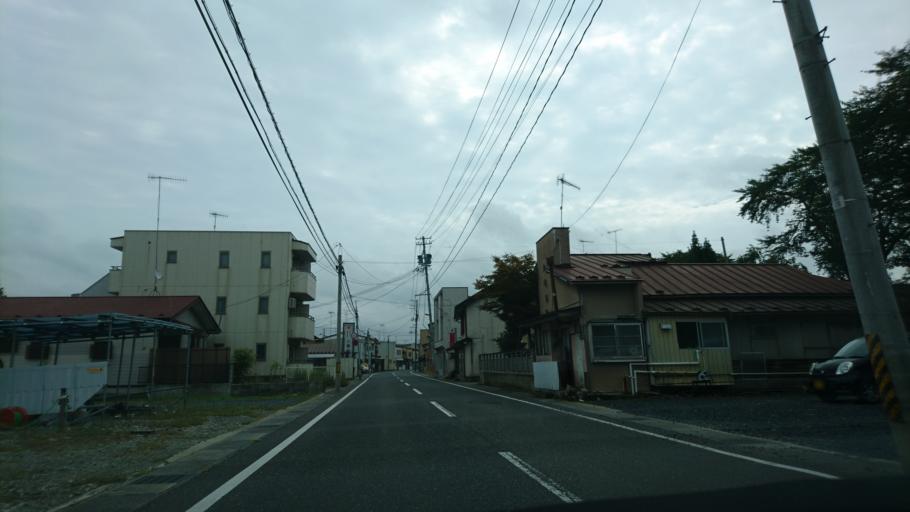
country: JP
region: Iwate
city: Ichinoseki
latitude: 38.7749
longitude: 141.1266
